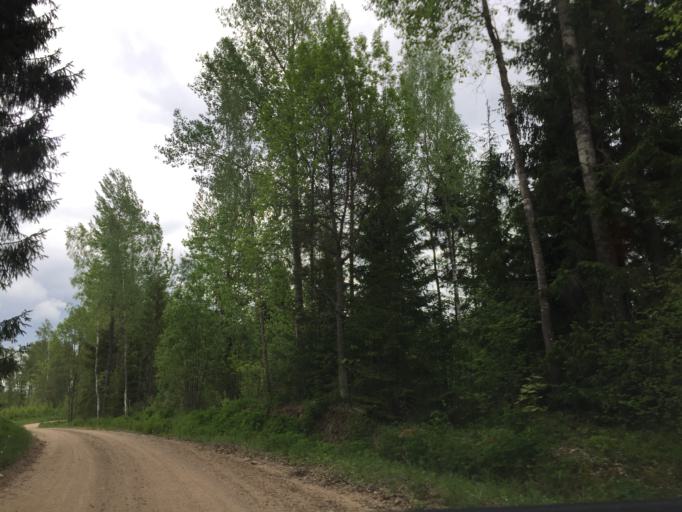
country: LV
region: Aglona
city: Aglona
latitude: 56.1769
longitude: 27.2508
